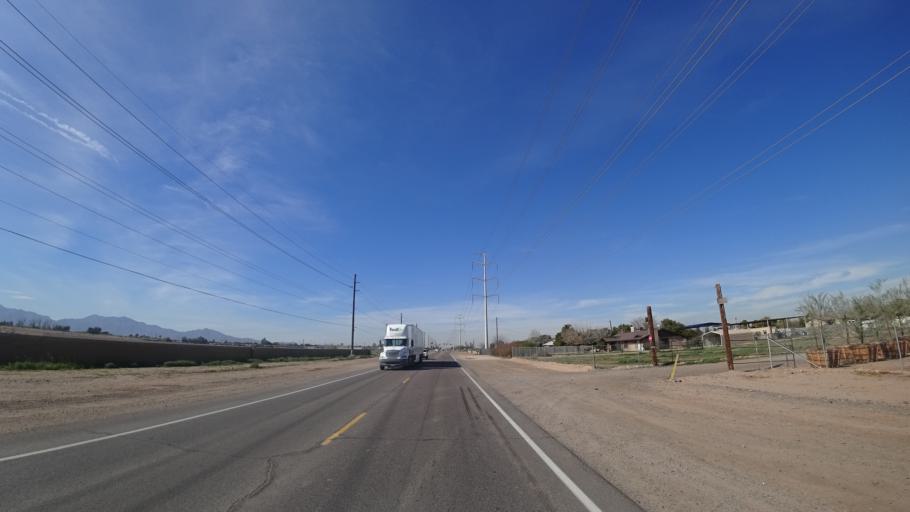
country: US
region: Arizona
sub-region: Maricopa County
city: Laveen
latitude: 33.4084
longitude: -112.2005
